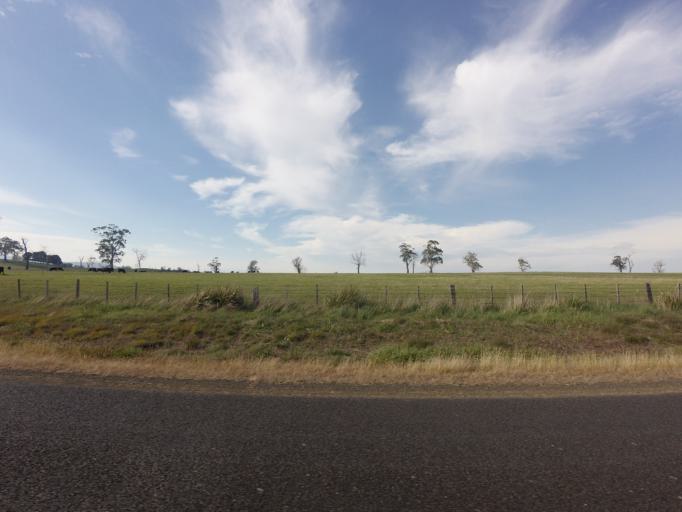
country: AU
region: Tasmania
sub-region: Northern Midlands
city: Longford
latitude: -41.5432
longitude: 146.9917
